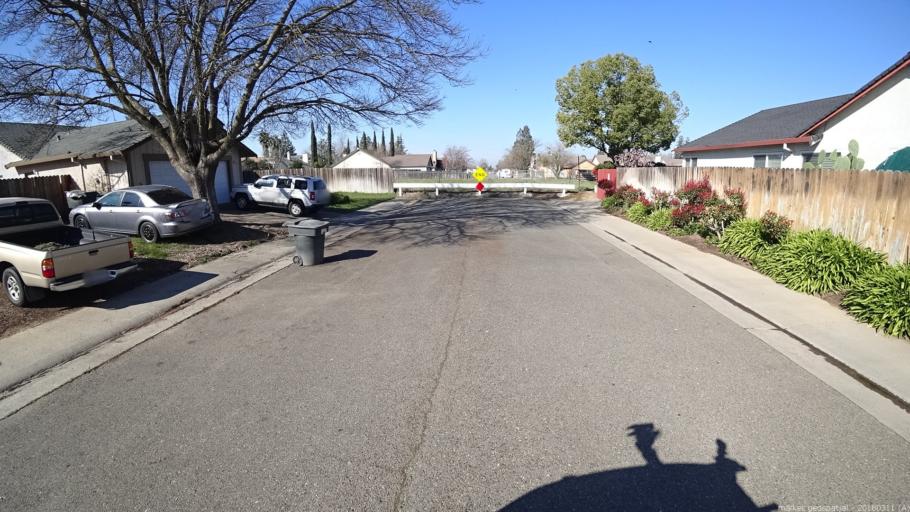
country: US
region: California
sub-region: Sacramento County
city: Florin
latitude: 38.4639
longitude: -121.3922
